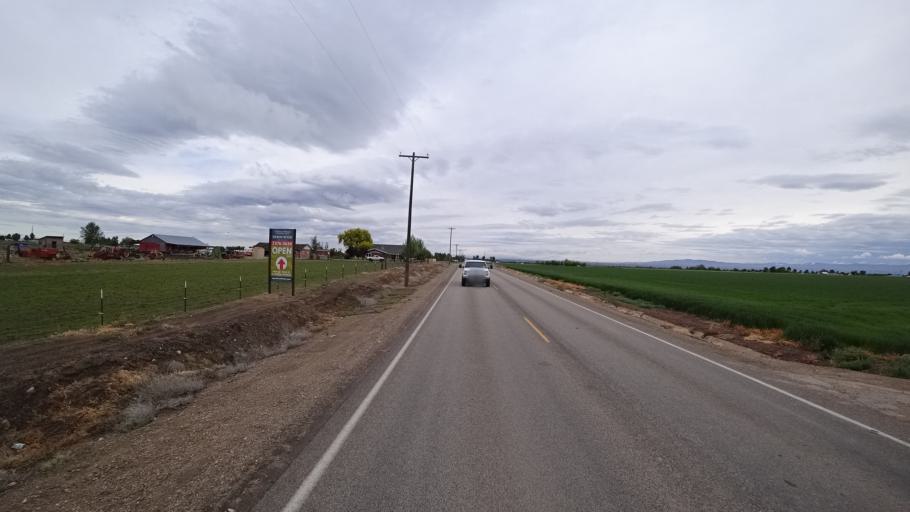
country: US
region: Idaho
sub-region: Ada County
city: Star
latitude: 43.6581
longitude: -116.4935
